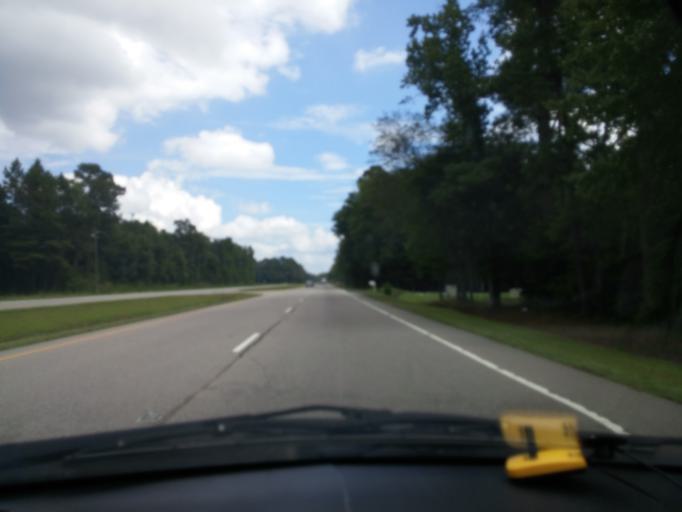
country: US
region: North Carolina
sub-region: Pitt County
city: Grifton
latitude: 35.3231
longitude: -77.5064
